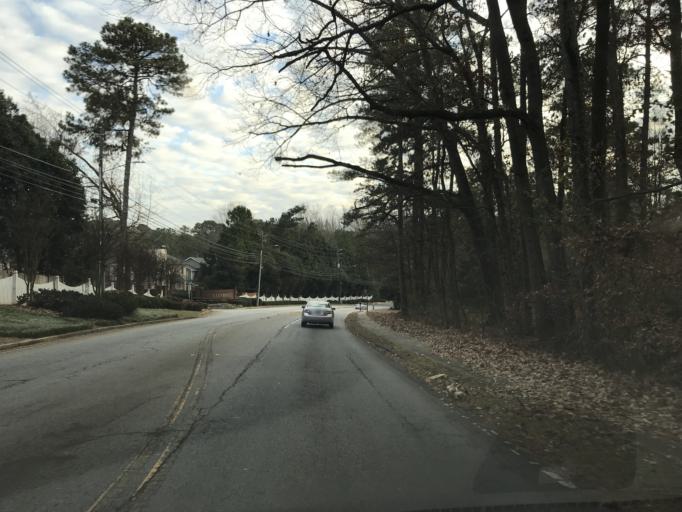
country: US
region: Georgia
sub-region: DeKalb County
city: Tucker
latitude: 33.8629
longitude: -84.2516
